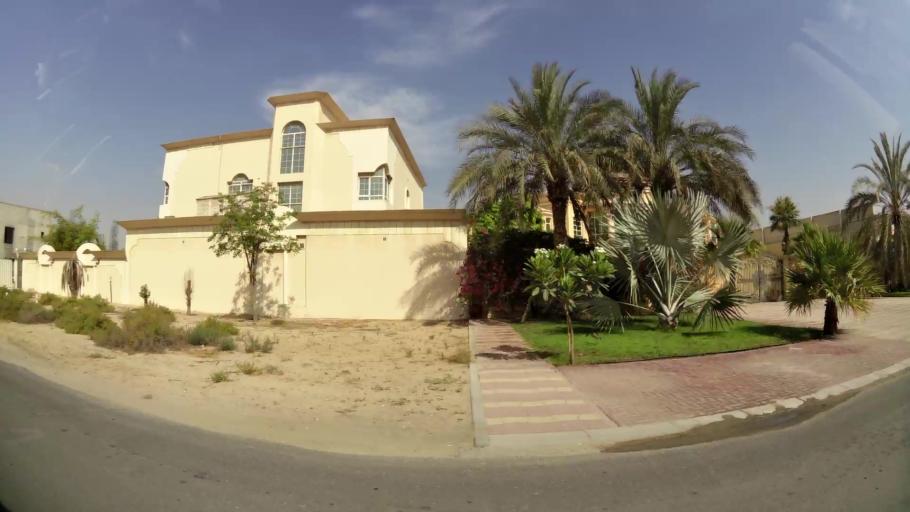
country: AE
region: Ash Shariqah
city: Sharjah
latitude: 25.2461
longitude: 55.4305
